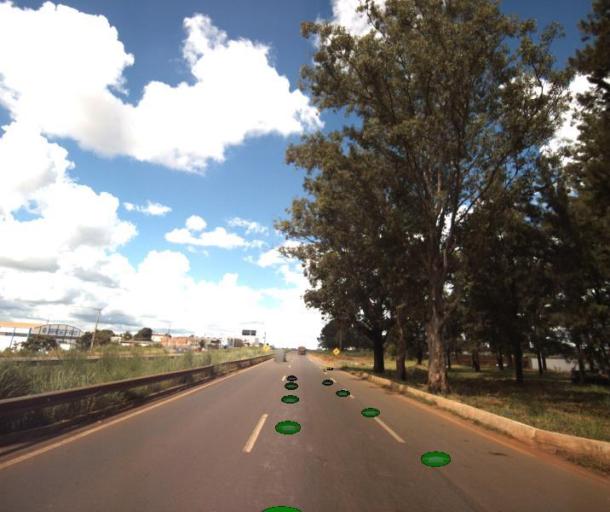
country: BR
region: Goias
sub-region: Anapolis
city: Anapolis
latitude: -16.3536
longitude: -48.9249
